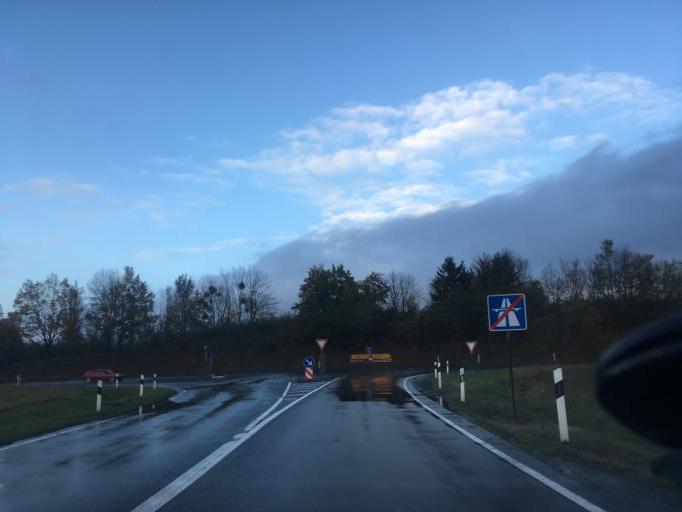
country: DE
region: Lower Saxony
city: Norten-Hardenberg
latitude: 51.6292
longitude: 9.9163
